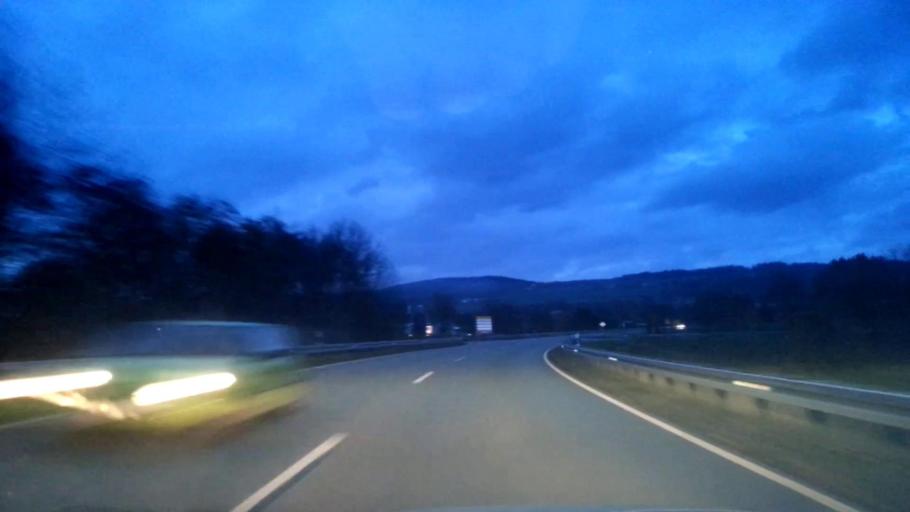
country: DE
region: Bavaria
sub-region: Upper Franconia
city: Seybothenreuth
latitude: 49.9381
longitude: 11.7385
